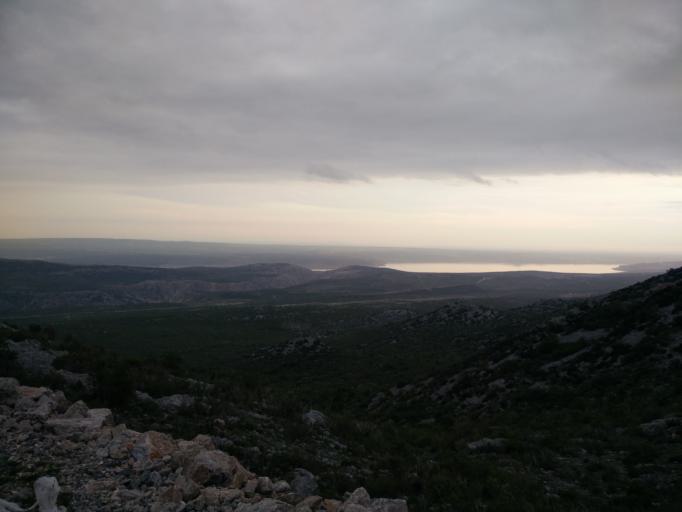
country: HR
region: Zadarska
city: Obrovac
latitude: 44.2494
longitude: 15.6370
